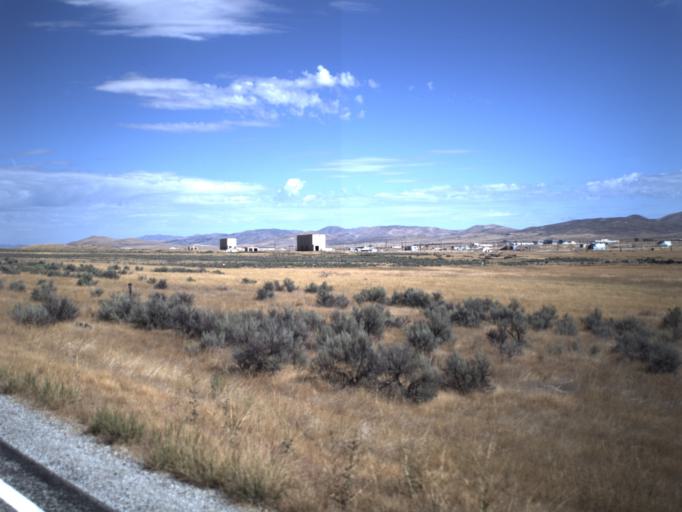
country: US
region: Utah
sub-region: Box Elder County
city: Tremonton
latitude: 41.6988
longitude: -112.4465
